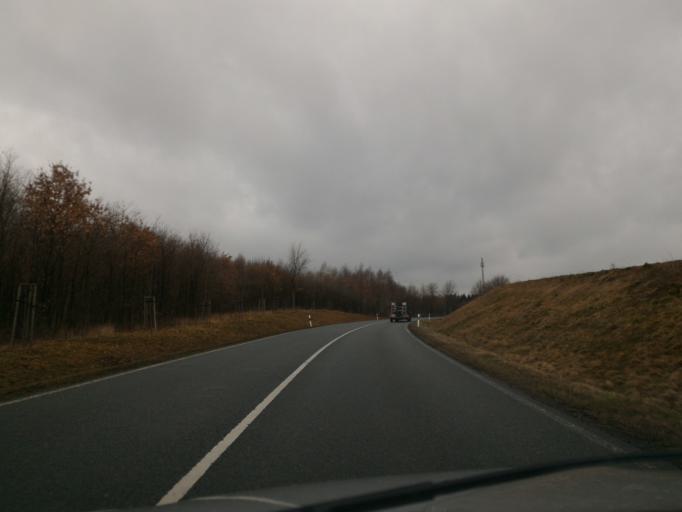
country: DE
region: Saxony
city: Neugersdorf
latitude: 50.9841
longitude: 14.6270
